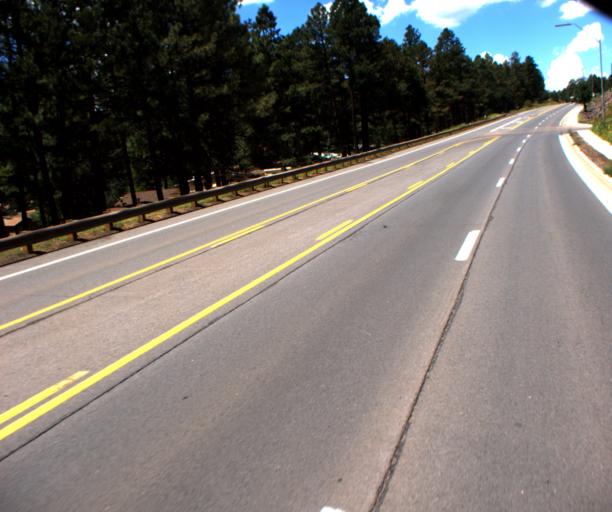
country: US
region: Arizona
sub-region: Coconino County
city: Flagstaff
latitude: 35.1880
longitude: -111.6845
